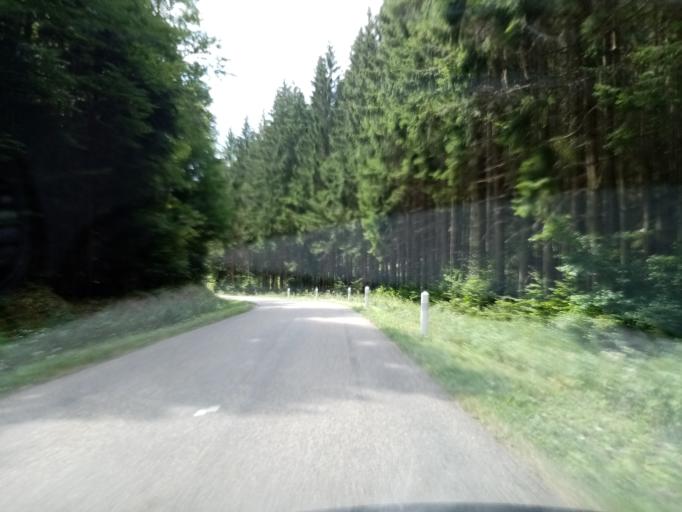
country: FR
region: Alsace
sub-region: Departement du Bas-Rhin
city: Dambach-la-Ville
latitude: 48.3404
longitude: 7.3794
